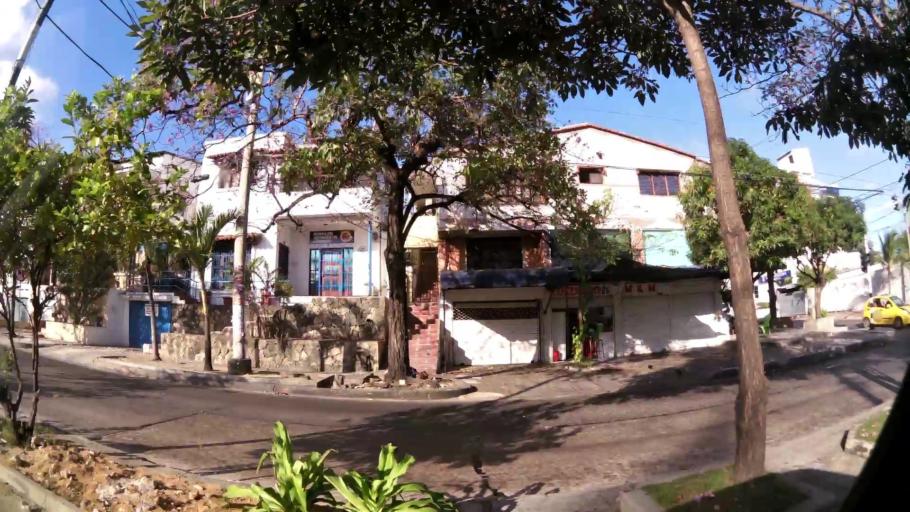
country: CO
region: Atlantico
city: Barranquilla
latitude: 10.9992
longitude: -74.8144
